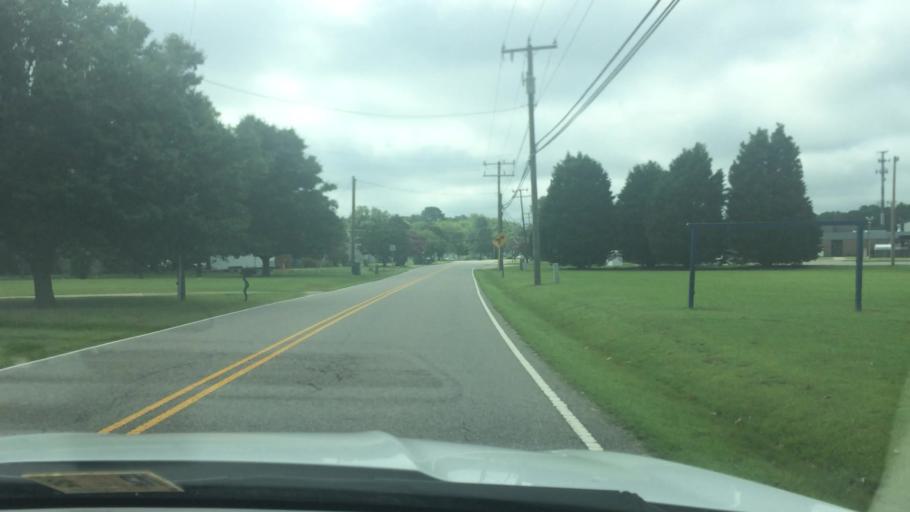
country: US
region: Virginia
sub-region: City of Poquoson
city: Poquoson
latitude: 37.1265
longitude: -76.4351
